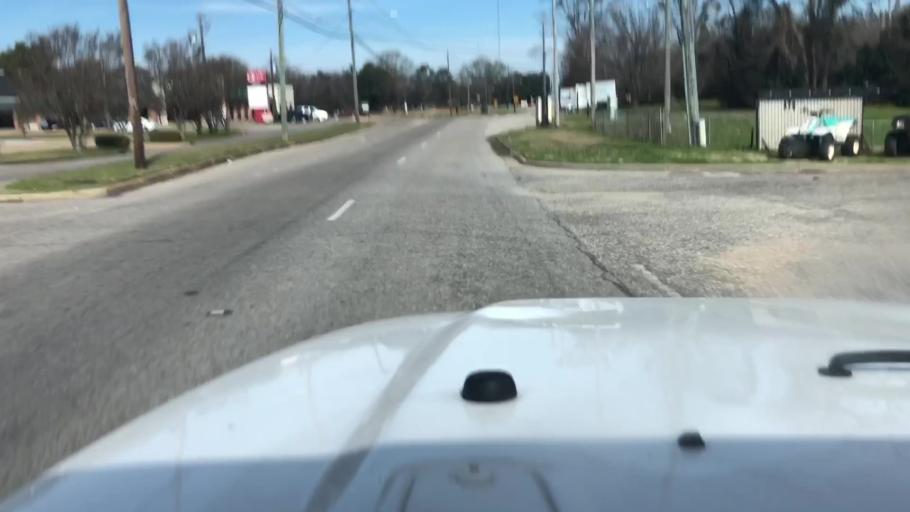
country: US
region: Alabama
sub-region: Montgomery County
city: Montgomery
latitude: 32.3850
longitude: -86.1991
